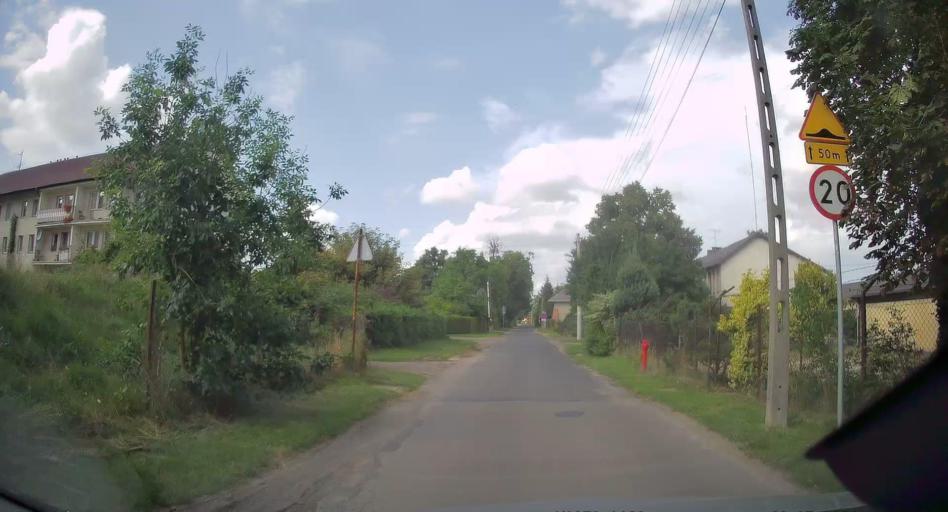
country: PL
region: Lodz Voivodeship
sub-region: Powiat brzezinski
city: Rogow
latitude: 51.8178
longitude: 19.8975
